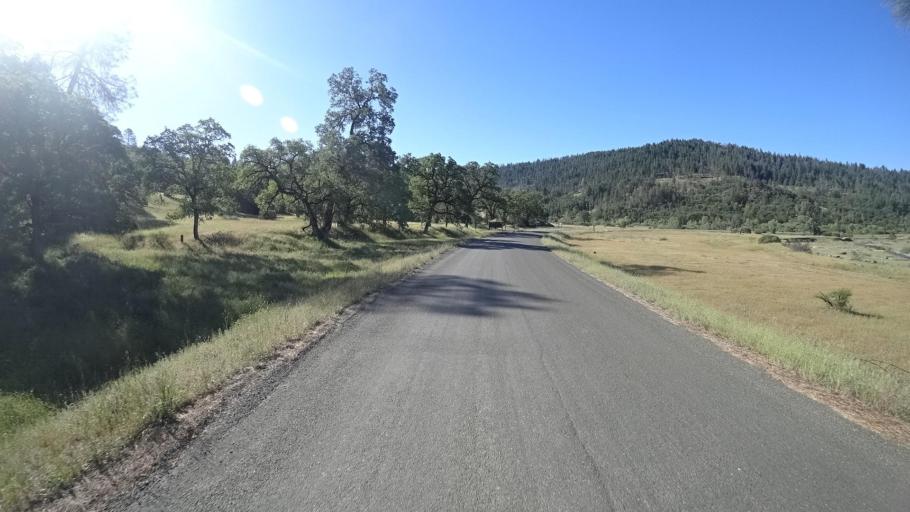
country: US
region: California
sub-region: Lake County
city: Upper Lake
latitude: 39.4148
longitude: -122.9747
